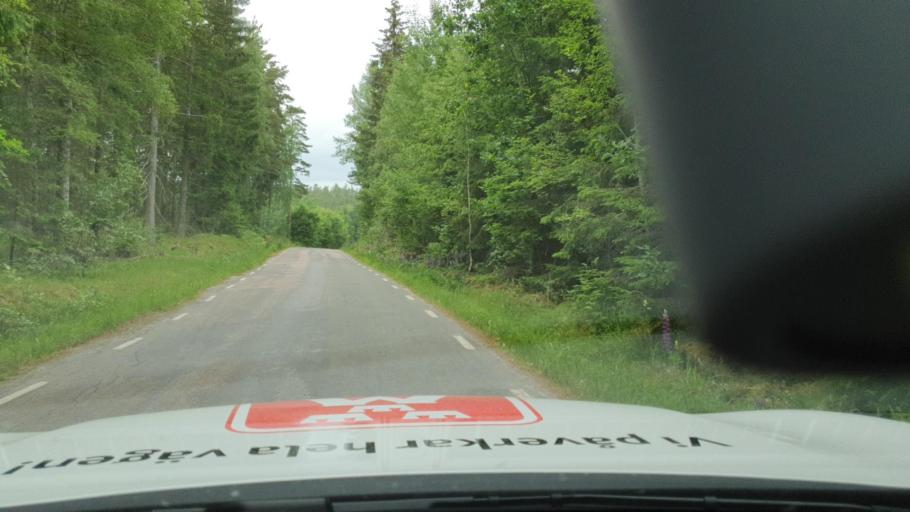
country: SE
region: Vaestra Goetaland
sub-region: Tidaholms Kommun
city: Tidaholm
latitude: 58.1785
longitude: 14.0087
